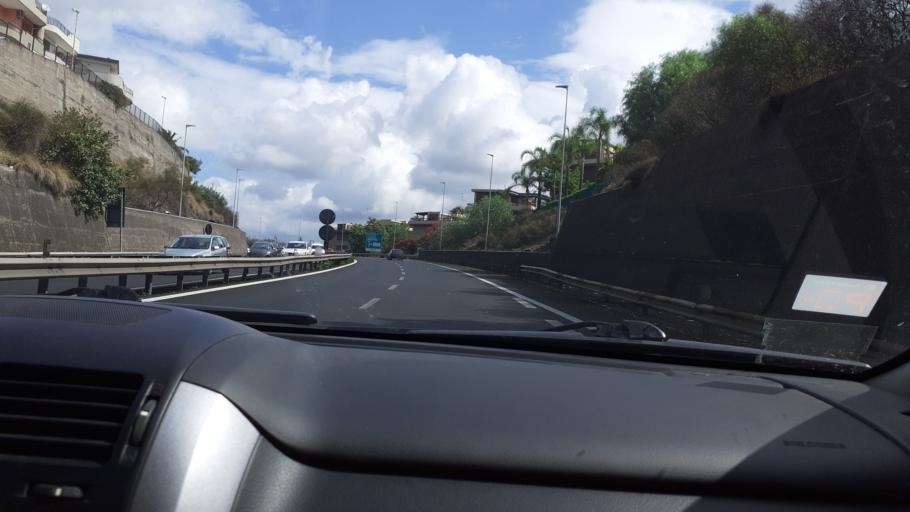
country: IT
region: Sicily
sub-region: Catania
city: Canalicchio
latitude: 37.5299
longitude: 15.0932
